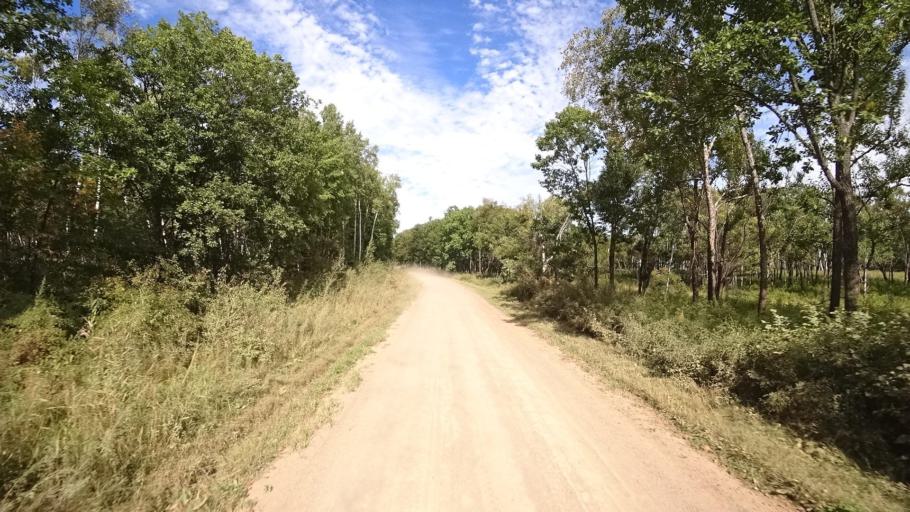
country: RU
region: Primorskiy
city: Yakovlevka
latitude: 44.3920
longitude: 133.5502
